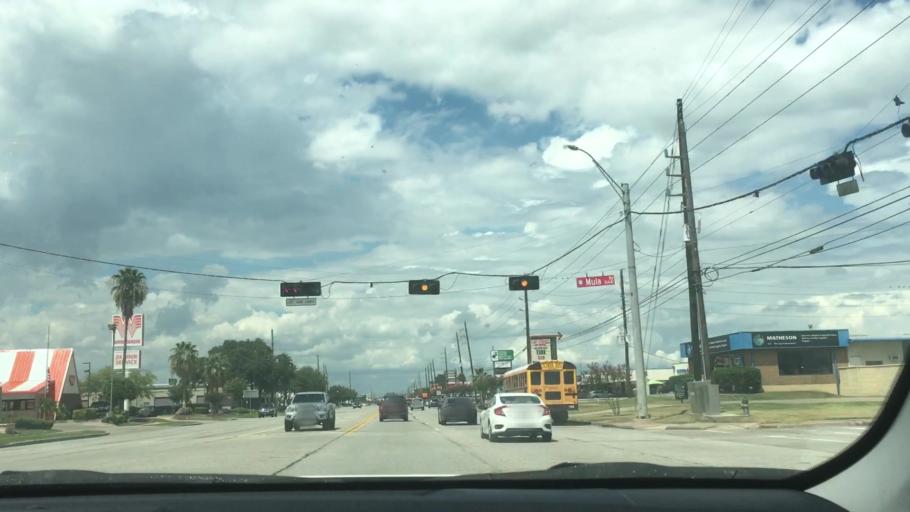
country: US
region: Texas
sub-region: Fort Bend County
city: Stafford
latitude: 29.6324
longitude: -95.5650
